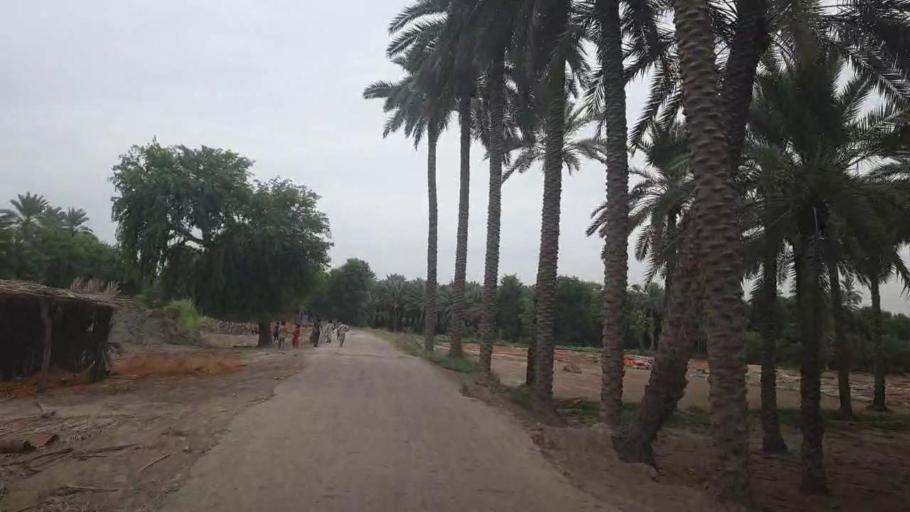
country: PK
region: Sindh
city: Khairpur
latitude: 27.6003
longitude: 68.7579
